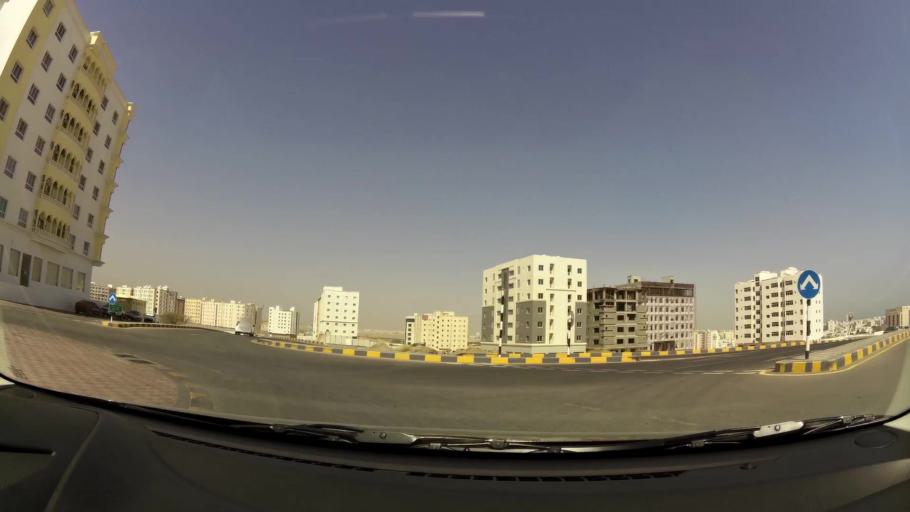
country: OM
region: Muhafazat Masqat
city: Bawshar
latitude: 23.5759
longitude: 58.4125
